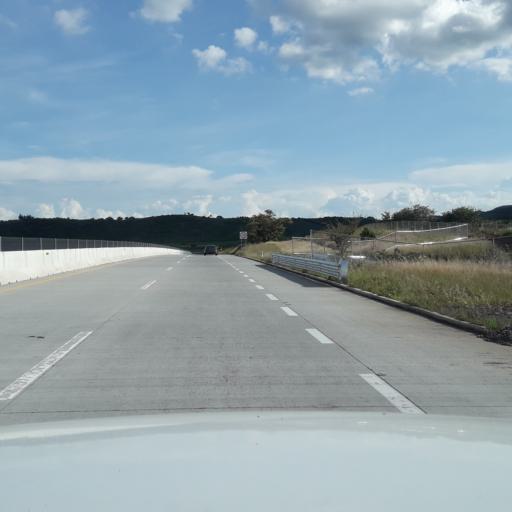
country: MX
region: Jalisco
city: Arenal
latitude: 20.7842
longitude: -103.7135
